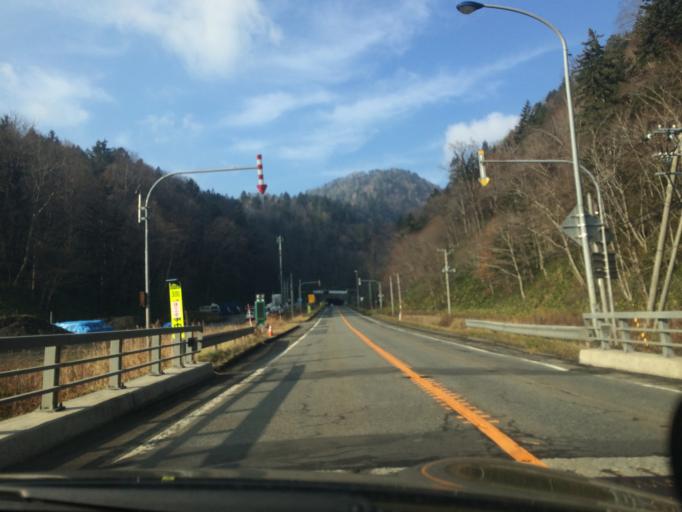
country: JP
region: Hokkaido
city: Shimo-furano
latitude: 42.9096
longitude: 142.3516
